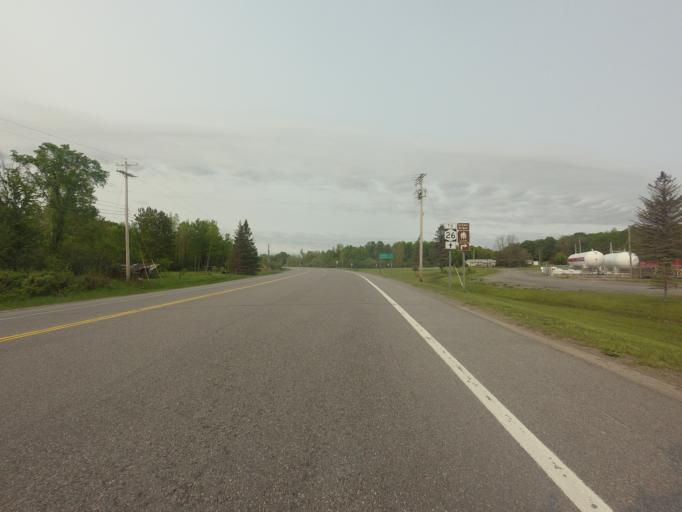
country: US
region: New York
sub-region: Jefferson County
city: Carthage
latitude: 44.0347
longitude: -75.5799
